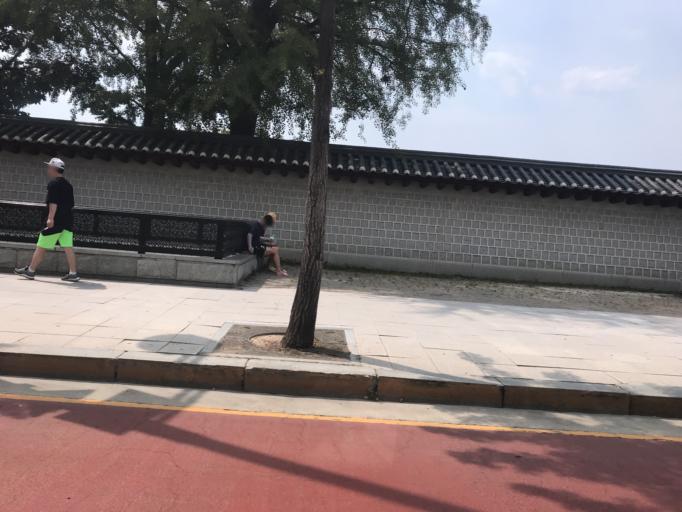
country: KR
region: Seoul
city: Seoul
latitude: 37.5762
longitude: 126.9792
